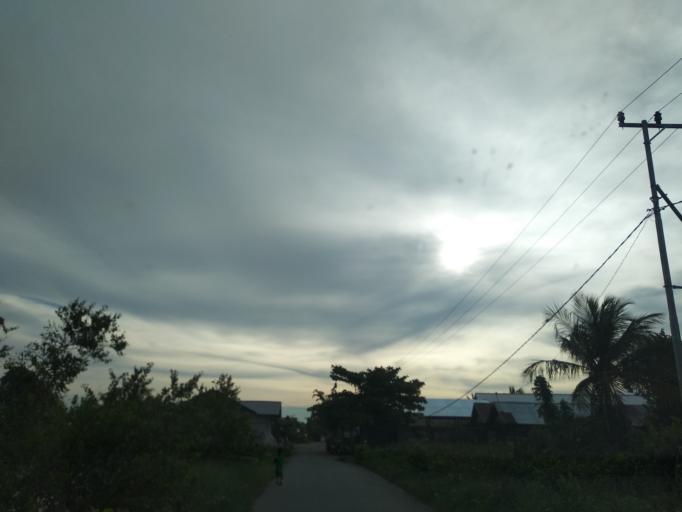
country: ID
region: South Kalimantan
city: Aluhaluh
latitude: -3.4655
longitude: 114.5485
